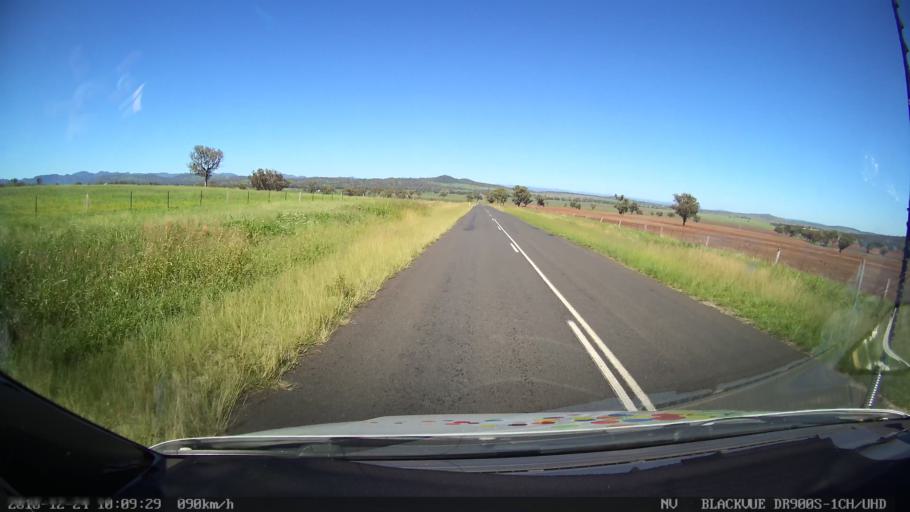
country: AU
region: New South Wales
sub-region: Liverpool Plains
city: Quirindi
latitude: -31.6637
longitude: 150.6903
